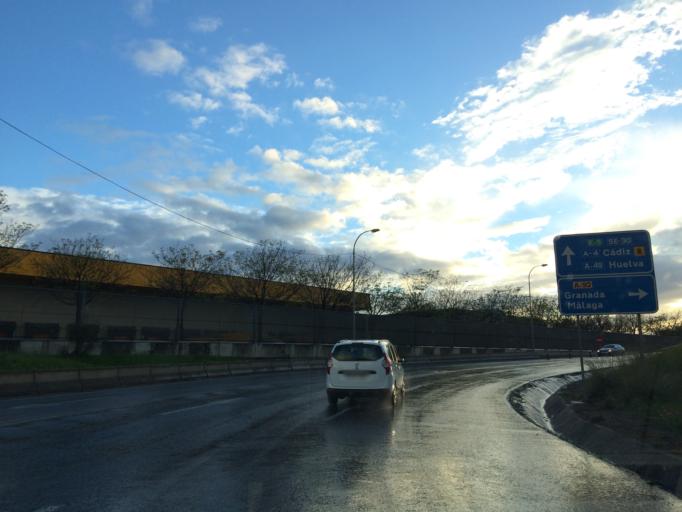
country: ES
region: Andalusia
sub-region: Provincia de Sevilla
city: Sevilla
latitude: 37.3858
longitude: -5.9349
